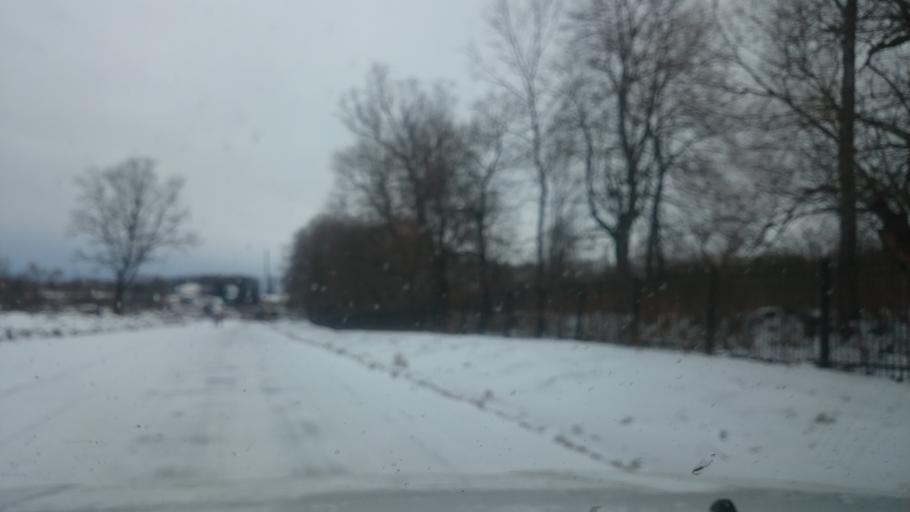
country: RU
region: Tula
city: Pervomayskiy
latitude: 54.0758
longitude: 37.5343
